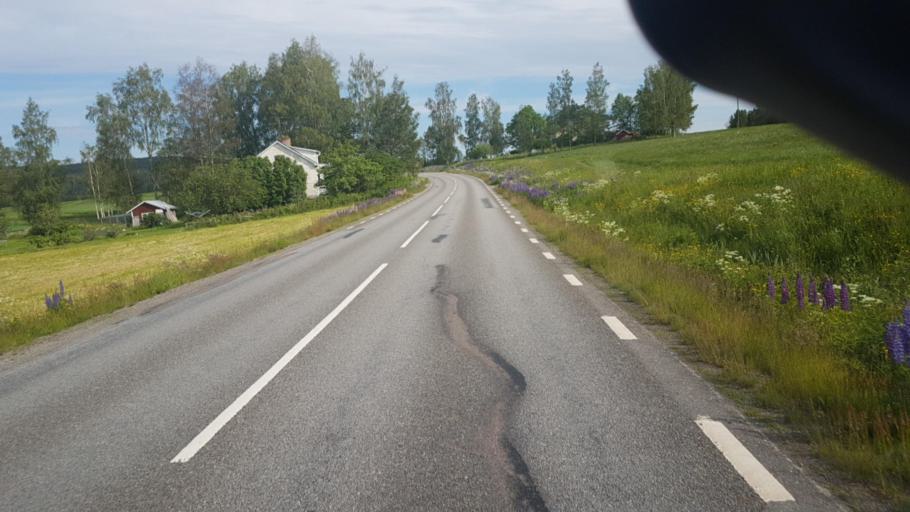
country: SE
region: Vaermland
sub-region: Arvika Kommun
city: Arvika
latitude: 59.7488
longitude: 12.5540
